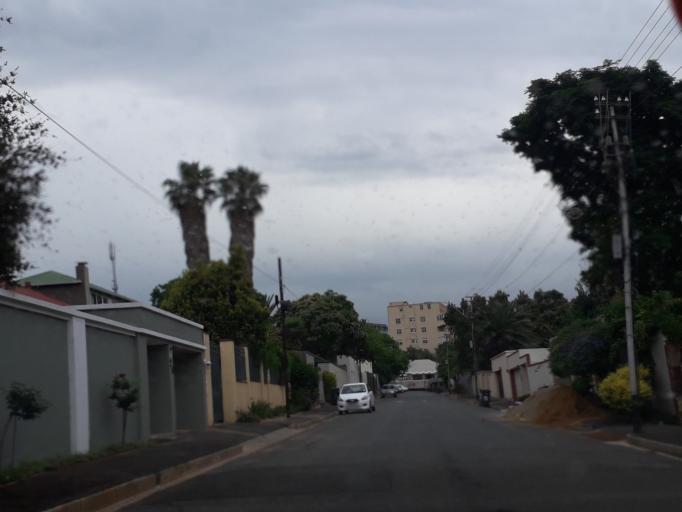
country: ZA
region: Gauteng
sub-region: City of Johannesburg Metropolitan Municipality
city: Johannesburg
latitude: -26.1662
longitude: 28.0774
